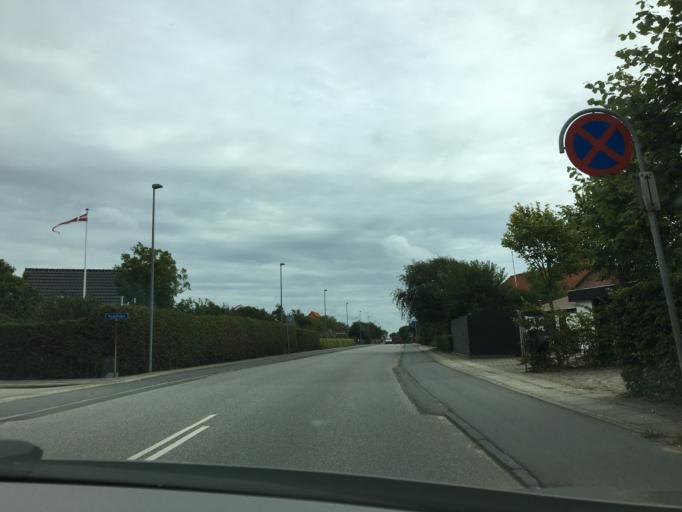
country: DK
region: Central Jutland
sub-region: Ringkobing-Skjern Kommune
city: Ringkobing
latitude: 56.0844
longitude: 8.2545
